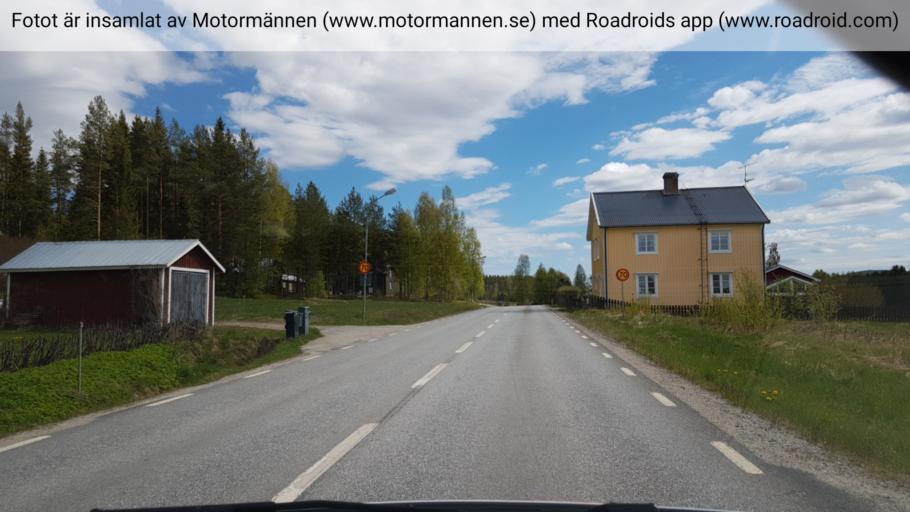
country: SE
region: Vaesterbotten
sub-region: Bjurholms Kommun
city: Bjurholm
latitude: 64.2430
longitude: 19.3270
